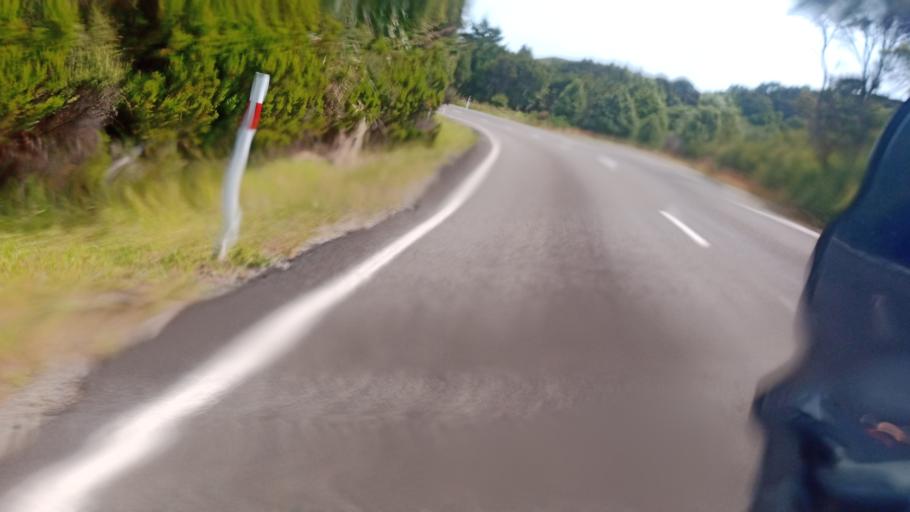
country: NZ
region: Bay of Plenty
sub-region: Opotiki District
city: Opotiki
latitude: -37.5744
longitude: 178.1341
